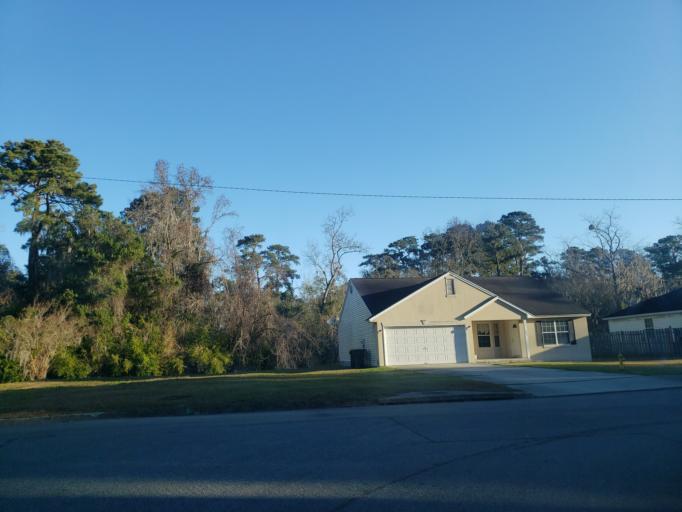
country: US
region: Georgia
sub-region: Chatham County
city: Isle of Hope
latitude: 32.0153
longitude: -81.0992
